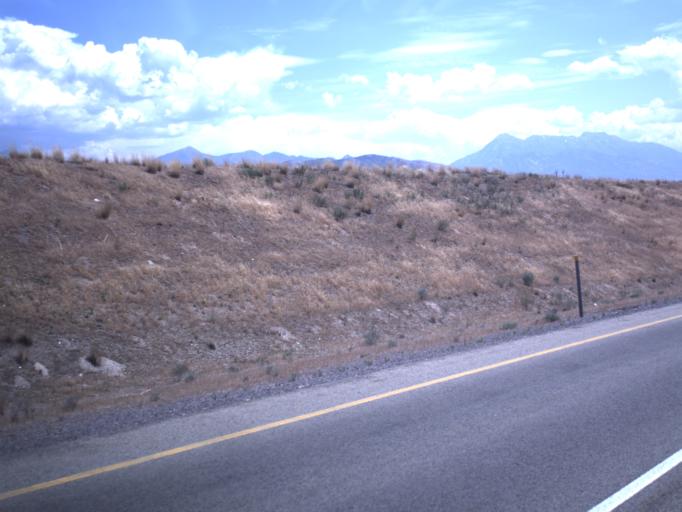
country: US
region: Utah
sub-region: Salt Lake County
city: Bluffdale
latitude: 40.4641
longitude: -111.9564
